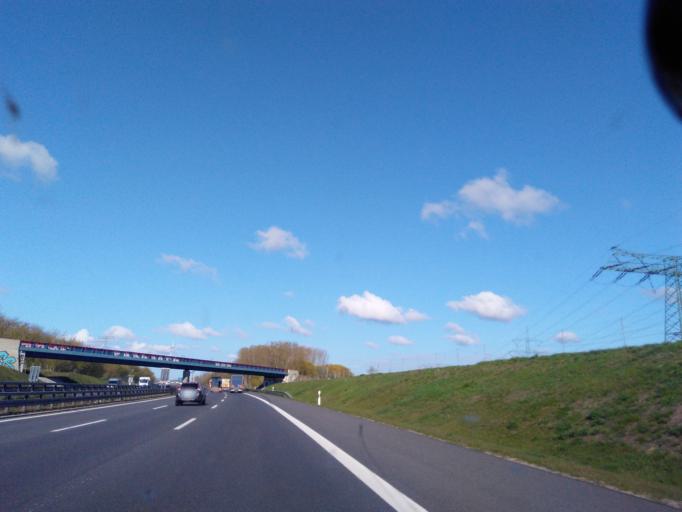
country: DE
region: Berlin
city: Karow
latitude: 52.6278
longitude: 13.4780
